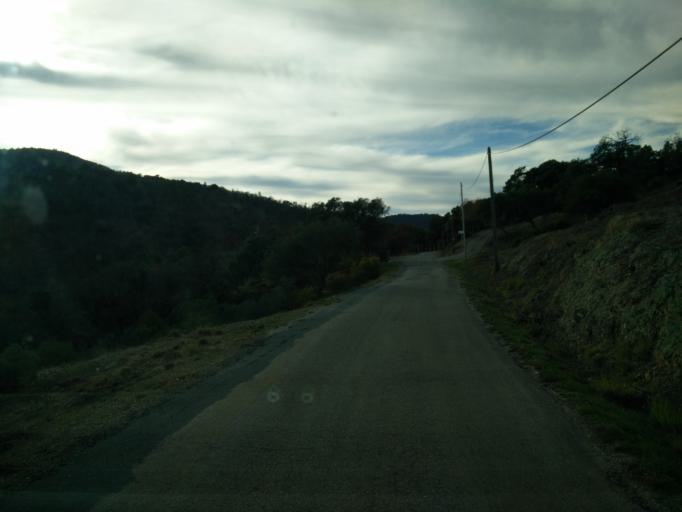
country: FR
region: Provence-Alpes-Cote d'Azur
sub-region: Departement du Var
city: Roquebrune-sur-Argens
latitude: 43.4353
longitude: 6.6363
